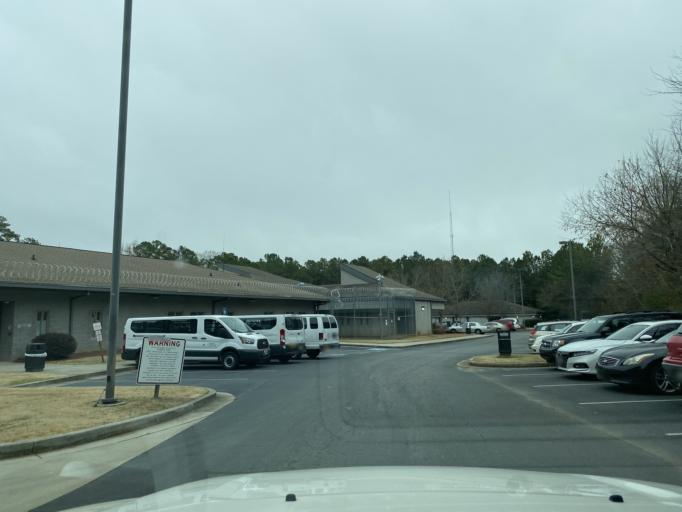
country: US
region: Georgia
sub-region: Cobb County
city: Fair Oaks
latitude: 33.9160
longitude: -84.5806
